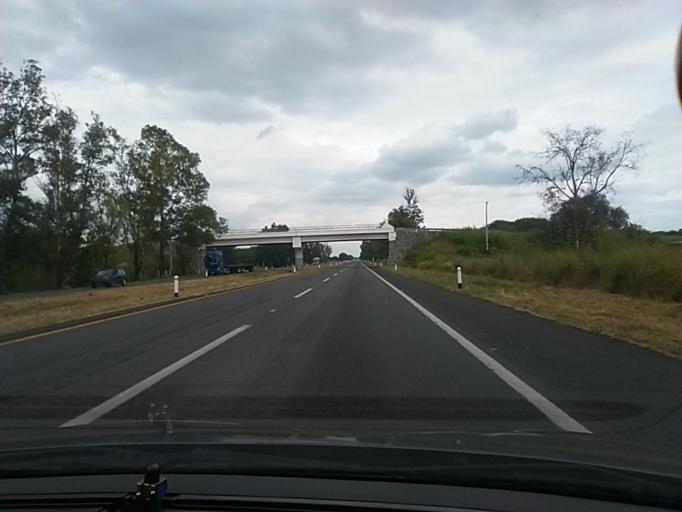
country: MX
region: Jalisco
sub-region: Ocotlan
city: Joconoxtle (La Tuna)
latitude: 20.3798
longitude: -102.6922
